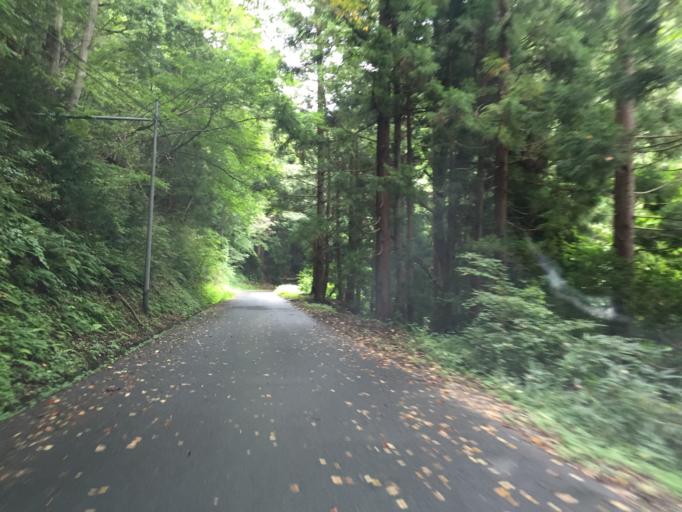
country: JP
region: Fukushima
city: Fukushima-shi
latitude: 37.7973
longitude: 140.3784
